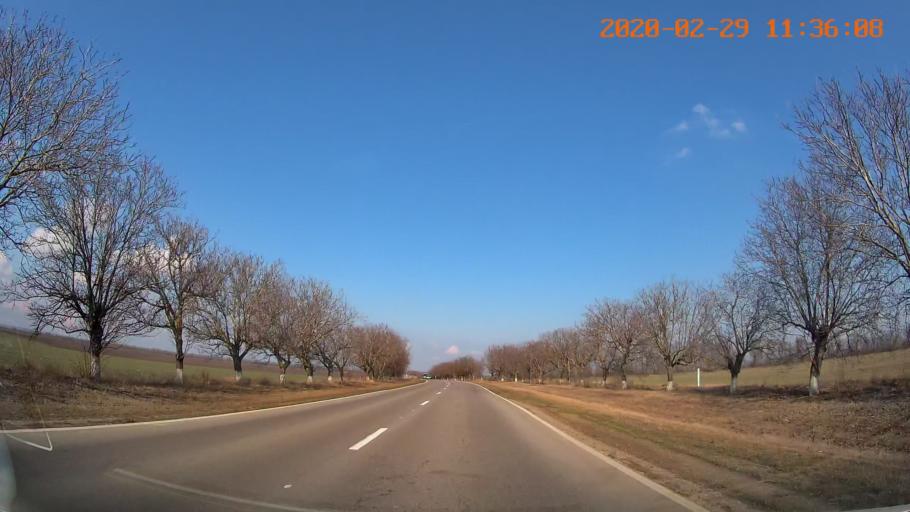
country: MD
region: Rezina
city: Saharna
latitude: 47.5913
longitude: 29.0586
